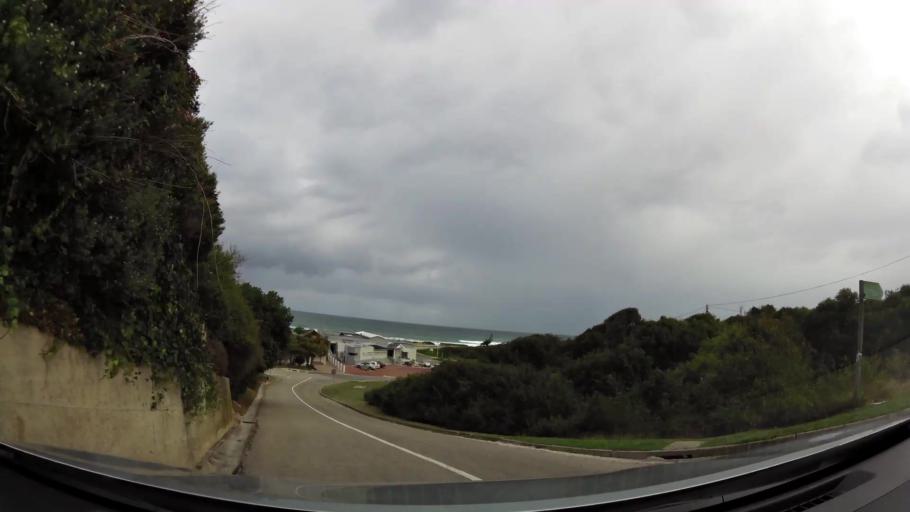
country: ZA
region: Western Cape
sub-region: Eden District Municipality
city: George
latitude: -34.0488
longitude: 22.3154
